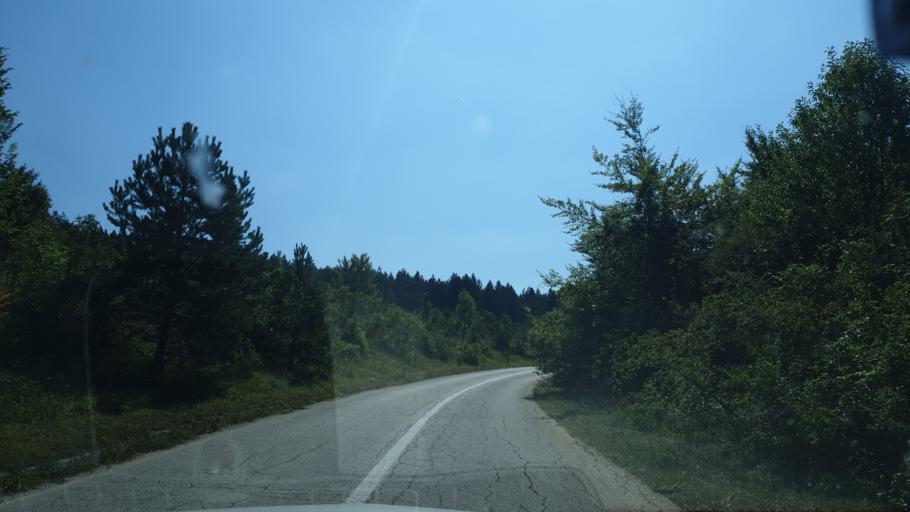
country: RS
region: Central Serbia
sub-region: Zlatiborski Okrug
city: Cajetina
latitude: 43.6785
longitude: 19.8511
